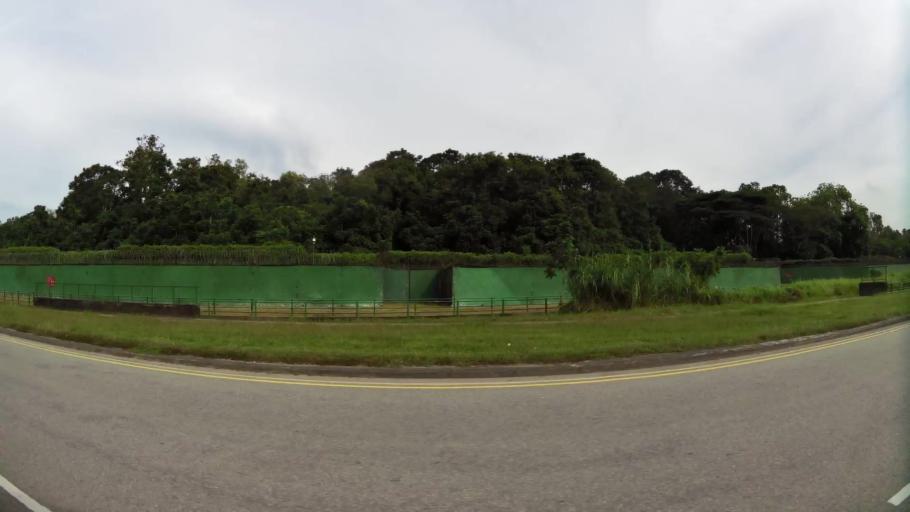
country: MY
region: Johor
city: Johor Bahru
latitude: 1.4013
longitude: 103.7003
